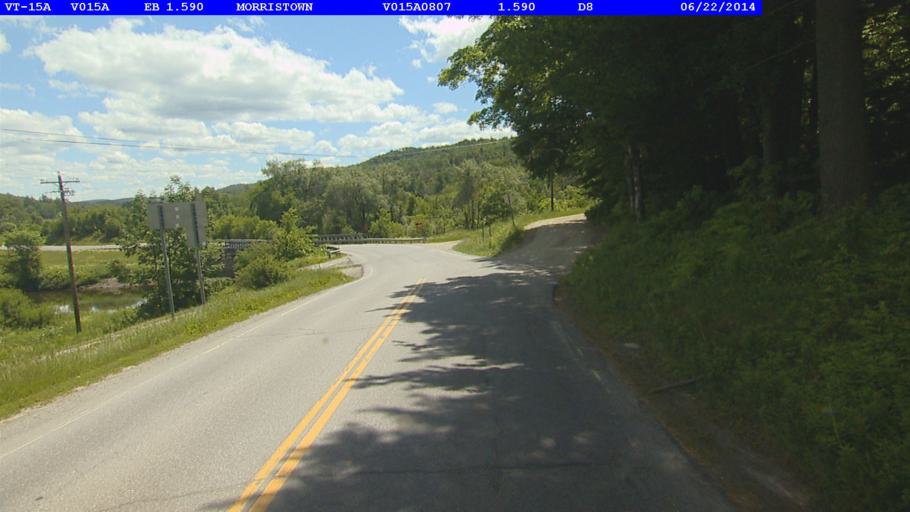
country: US
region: Vermont
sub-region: Lamoille County
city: Morrisville
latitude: 44.5642
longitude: -72.5673
